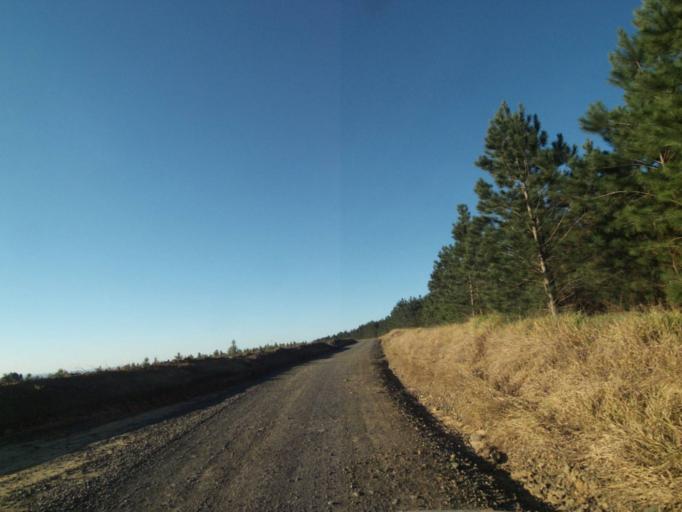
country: BR
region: Parana
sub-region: Telemaco Borba
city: Telemaco Borba
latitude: -24.4547
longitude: -50.6013
